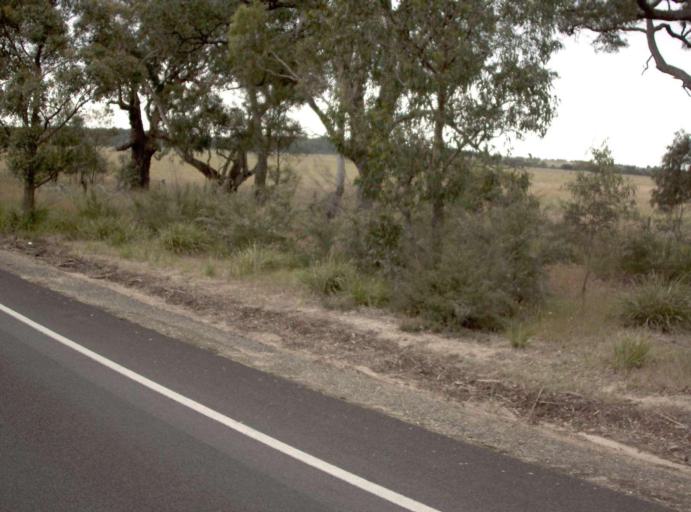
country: AU
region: Victoria
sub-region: Wellington
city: Sale
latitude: -38.3040
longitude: 147.0313
